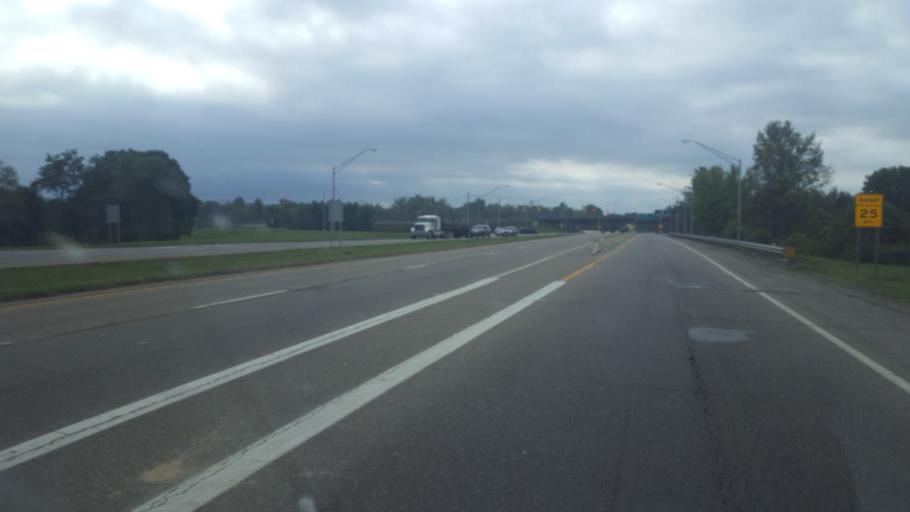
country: US
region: Ohio
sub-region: Tuscarawas County
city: Uhrichsville
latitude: 40.4073
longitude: -81.3494
